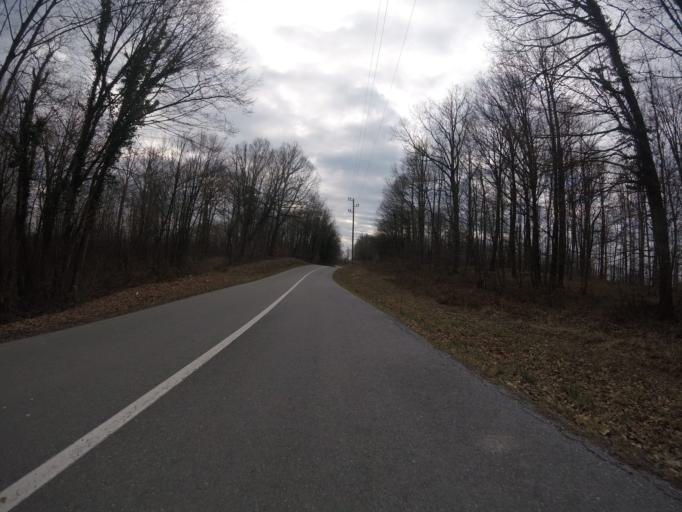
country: HR
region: Zagrebacka
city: Mraclin
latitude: 45.5475
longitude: 16.0553
